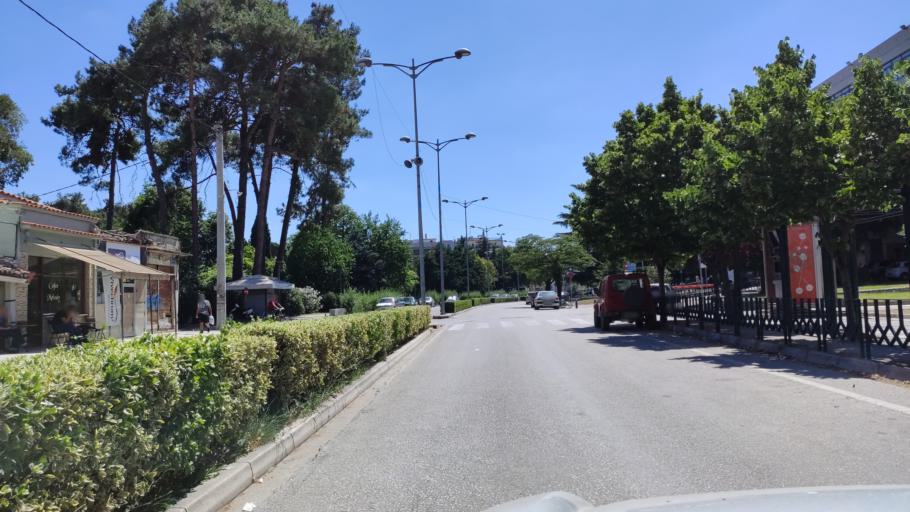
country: GR
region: East Macedonia and Thrace
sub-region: Nomos Rodopis
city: Komotini
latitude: 41.1185
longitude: 25.4078
